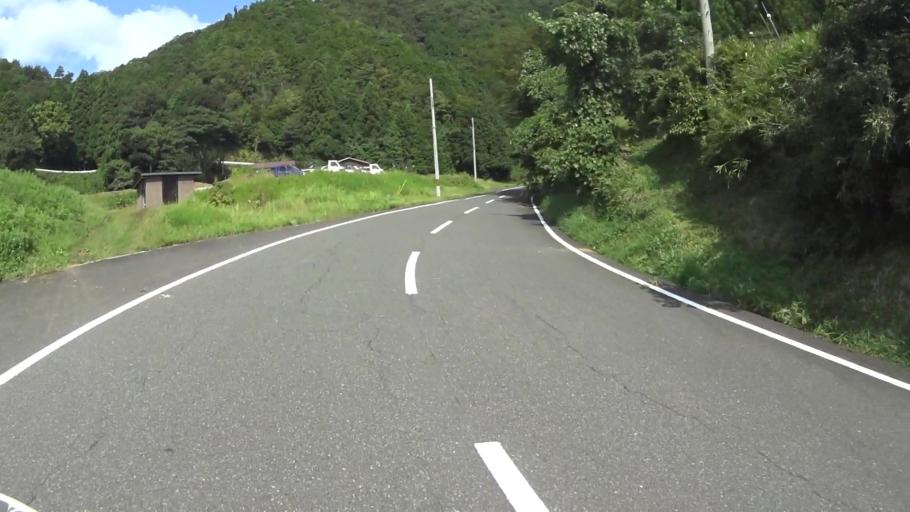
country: JP
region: Kyoto
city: Miyazu
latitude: 35.6759
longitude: 135.2707
